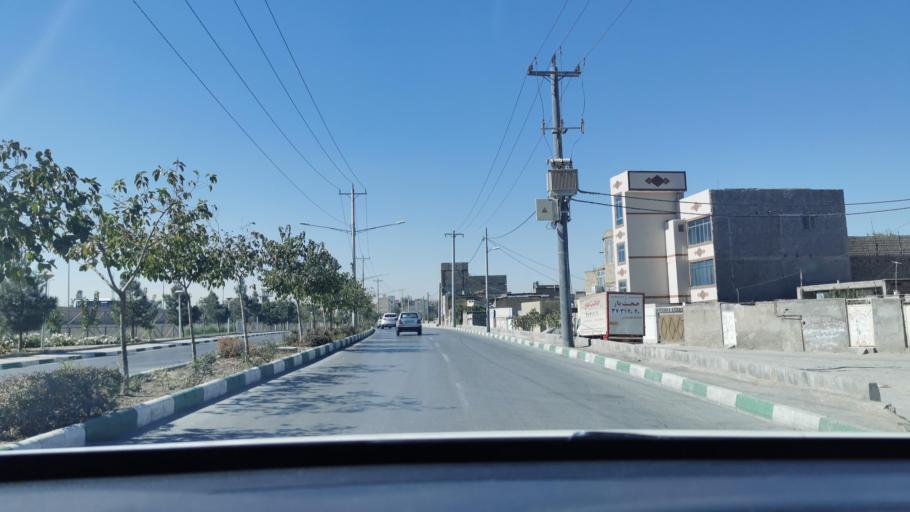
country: IR
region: Razavi Khorasan
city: Mashhad
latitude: 36.3352
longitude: 59.6161
